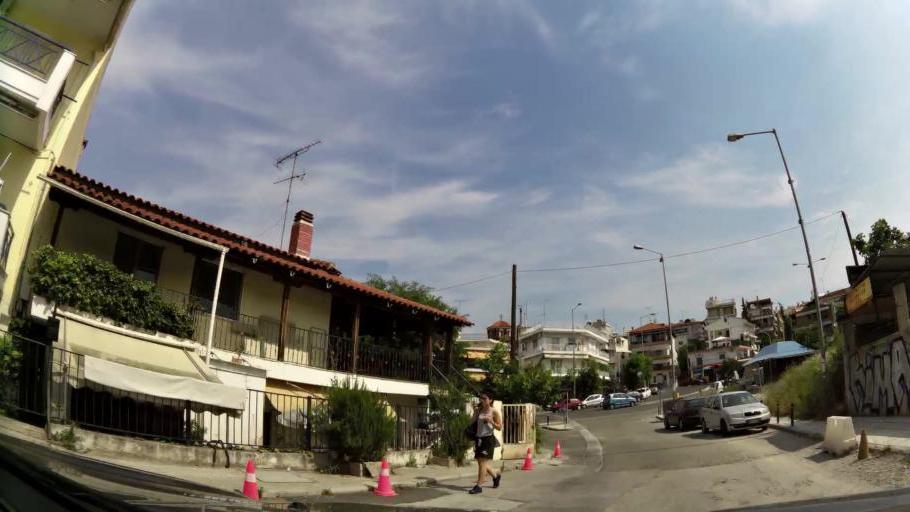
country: GR
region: Central Macedonia
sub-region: Nomos Thessalonikis
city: Agios Pavlos
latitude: 40.6471
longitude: 22.9606
